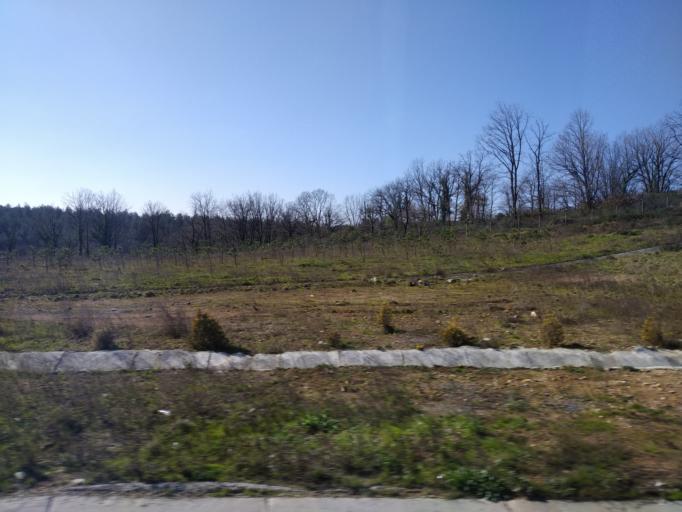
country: TR
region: Istanbul
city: Sancaktepe
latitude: 41.0606
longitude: 29.2755
